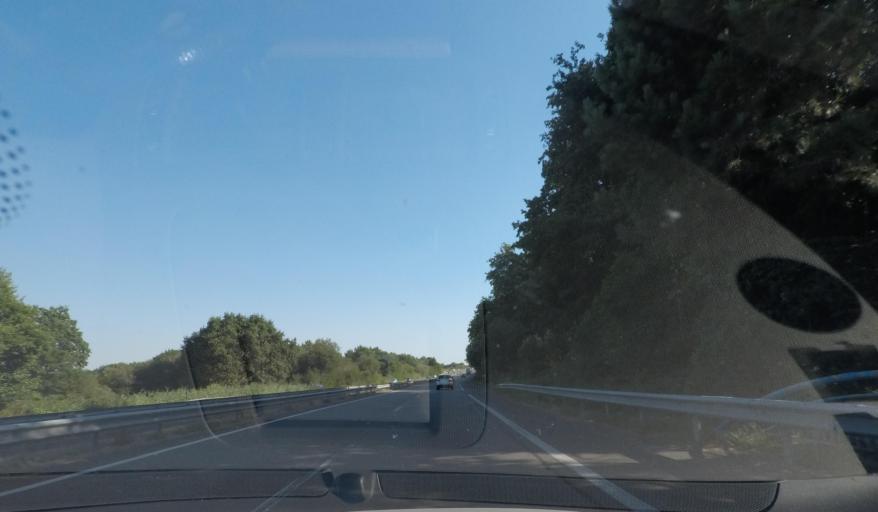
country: FR
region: Pays de la Loire
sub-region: Departement de la Loire-Atlantique
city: Saint-Brevin-les-Pins
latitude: 47.2257
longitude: -2.1532
